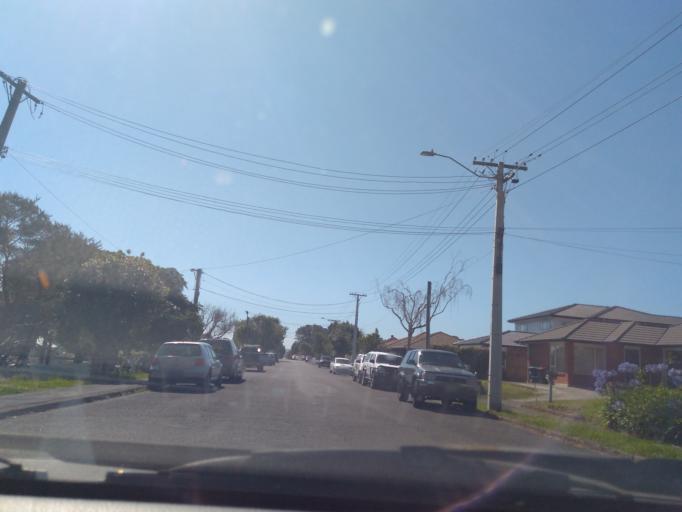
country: NZ
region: Auckland
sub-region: Auckland
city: Rosebank
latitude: -36.8789
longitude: 174.6983
